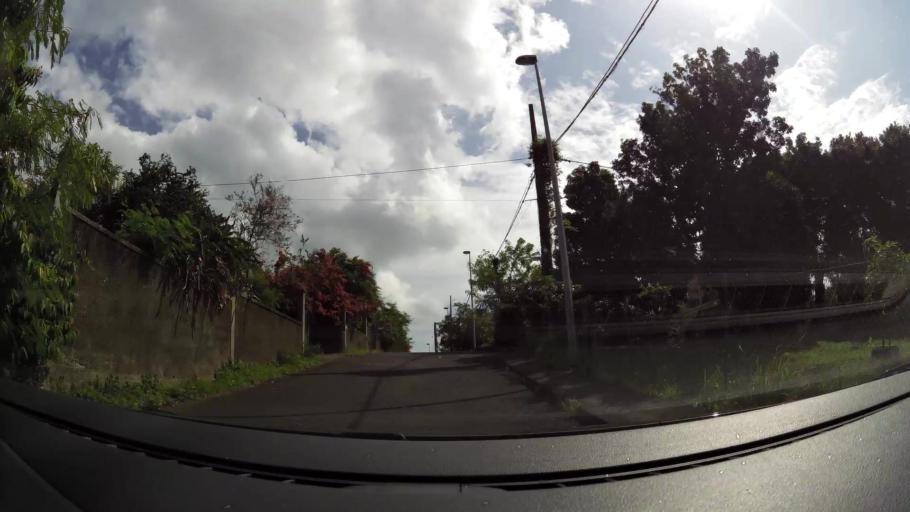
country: GP
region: Guadeloupe
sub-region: Guadeloupe
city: Basse-Terre
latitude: 16.0040
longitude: -61.7342
